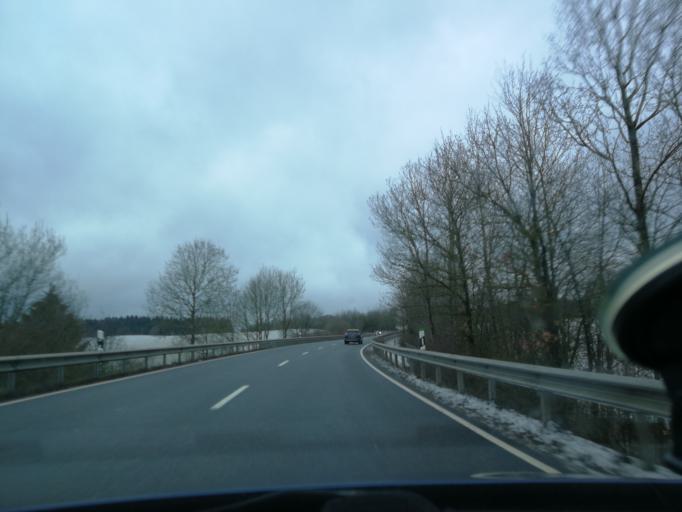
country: DE
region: Rheinland-Pfalz
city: Ohlenhard
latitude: 50.4460
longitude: 6.7121
